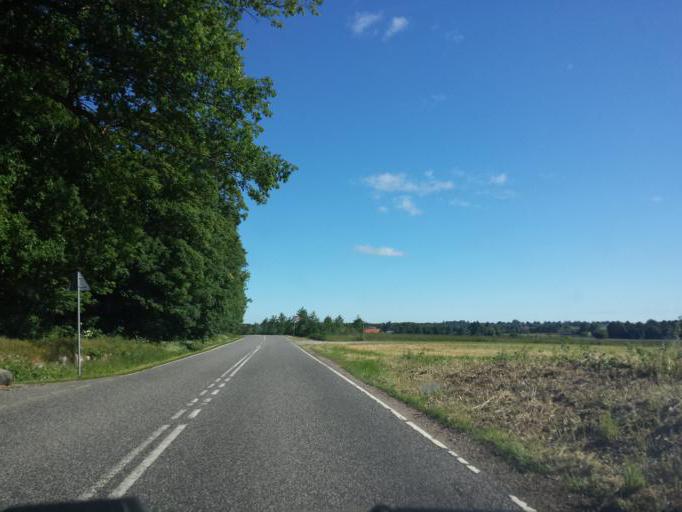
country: DK
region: Capital Region
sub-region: Egedal Kommune
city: Ganlose
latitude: 55.8071
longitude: 12.2619
